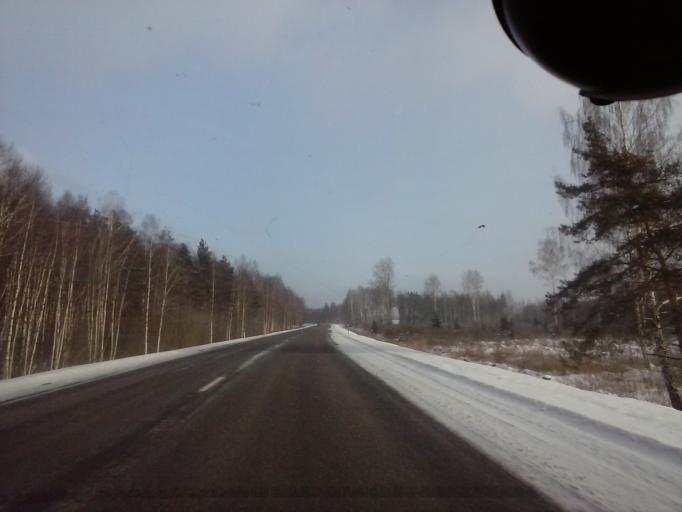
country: EE
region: Tartu
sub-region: Puhja vald
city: Puhja
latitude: 58.3289
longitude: 26.2173
